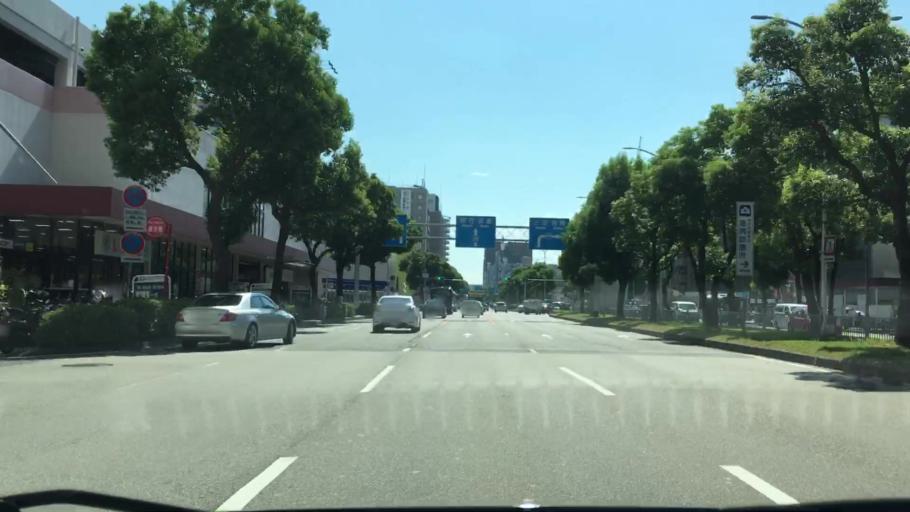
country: JP
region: Hyogo
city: Kobe
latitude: 34.6798
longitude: 135.1757
